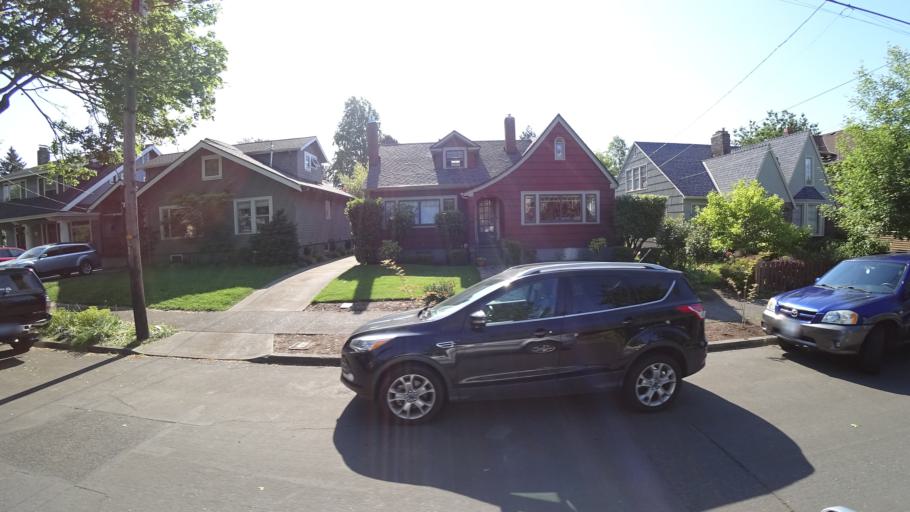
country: US
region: Oregon
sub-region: Multnomah County
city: Portland
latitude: 45.5474
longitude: -122.6431
